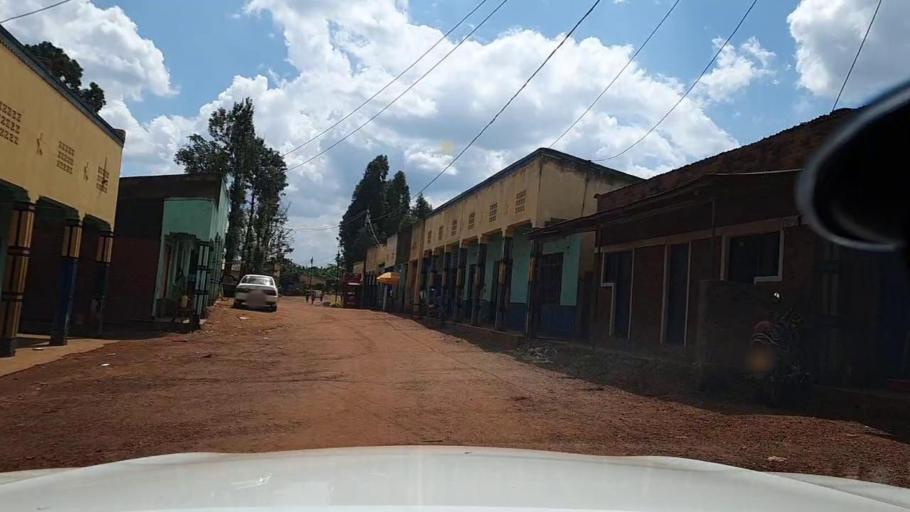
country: RW
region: Southern Province
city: Gitarama
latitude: -1.8357
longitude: 29.8338
